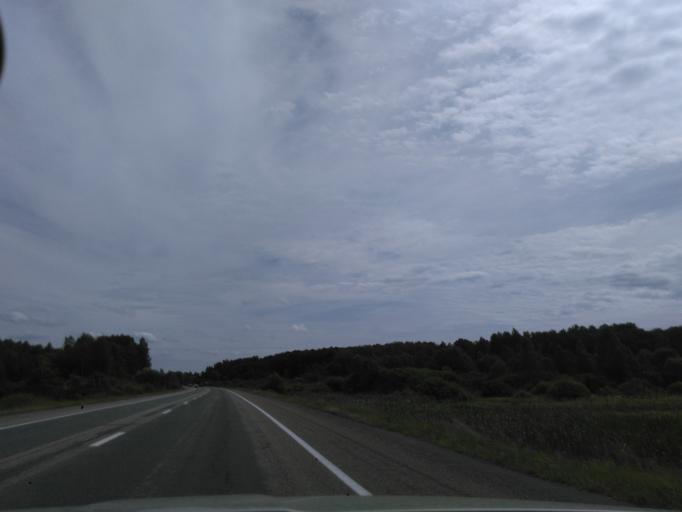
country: RU
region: Moskovskaya
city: Solnechnogorsk
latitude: 56.1476
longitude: 36.9347
